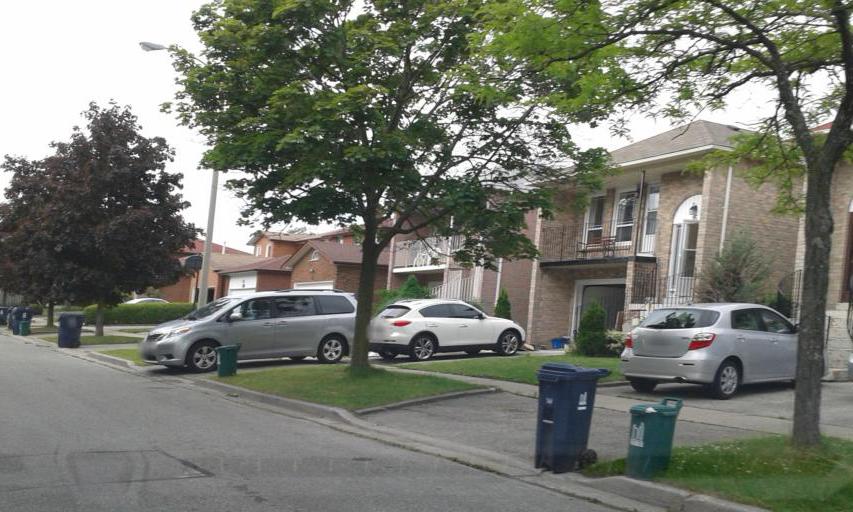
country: CA
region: Ontario
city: Scarborough
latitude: 43.8116
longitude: -79.2630
